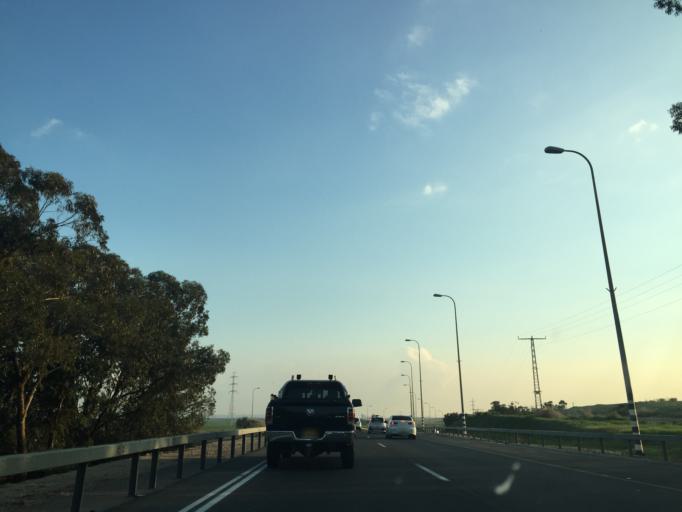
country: IL
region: Southern District
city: Lehavim
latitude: 31.4758
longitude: 34.7754
